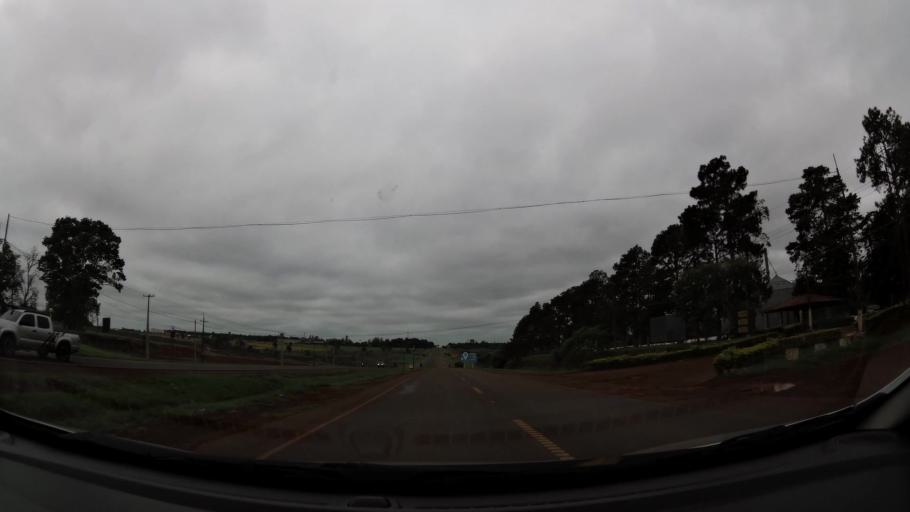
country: PY
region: Alto Parana
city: Colonia Yguazu
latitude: -25.4879
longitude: -54.8334
